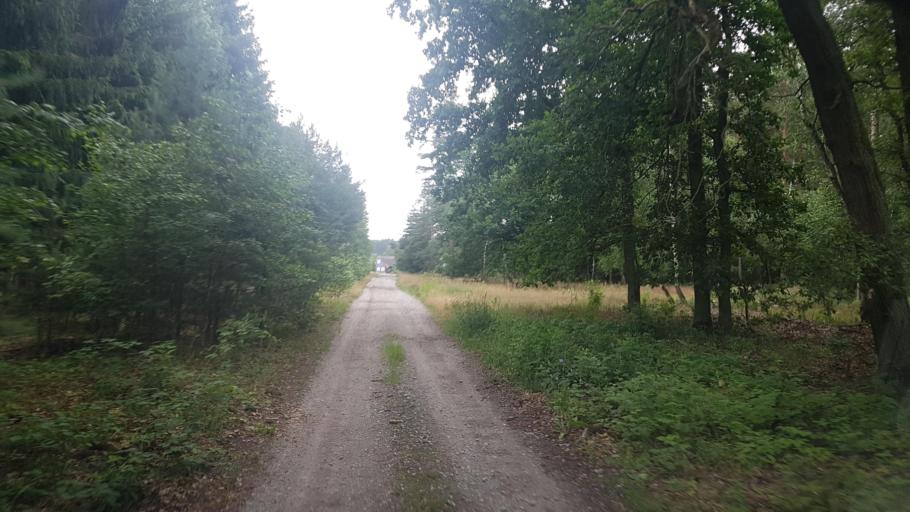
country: DE
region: Brandenburg
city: Crinitz
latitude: 51.7206
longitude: 13.8249
